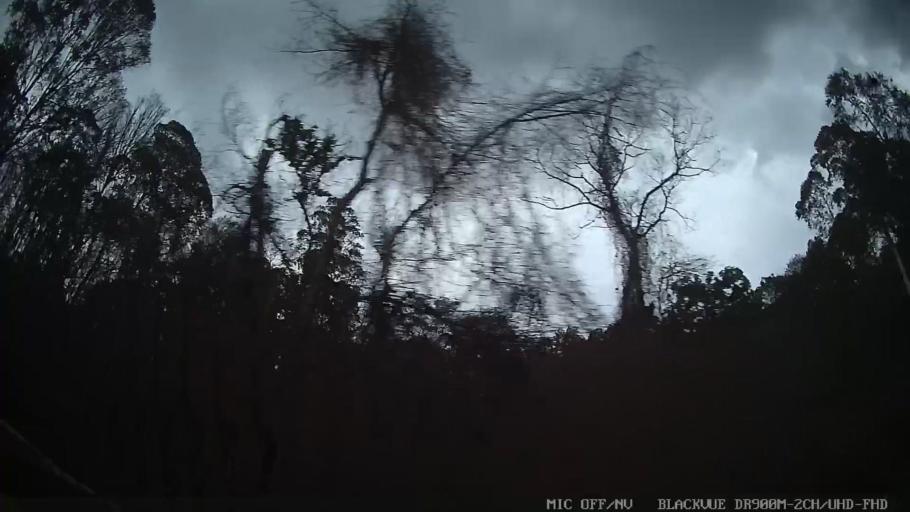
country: BR
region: Sao Paulo
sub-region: Amparo
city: Amparo
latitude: -22.7637
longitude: -46.7569
